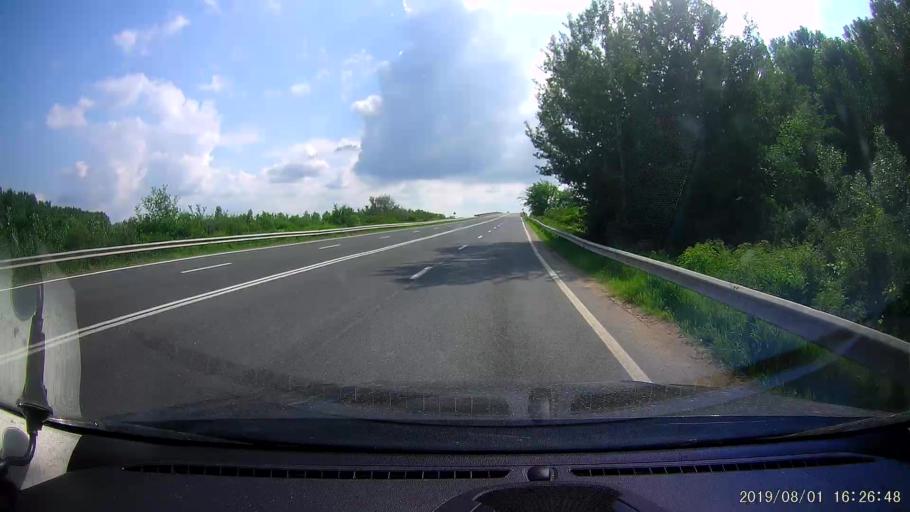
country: RO
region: Calarasi
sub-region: Municipiul Calarasi
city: Calarasi
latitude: 44.1724
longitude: 27.3180
